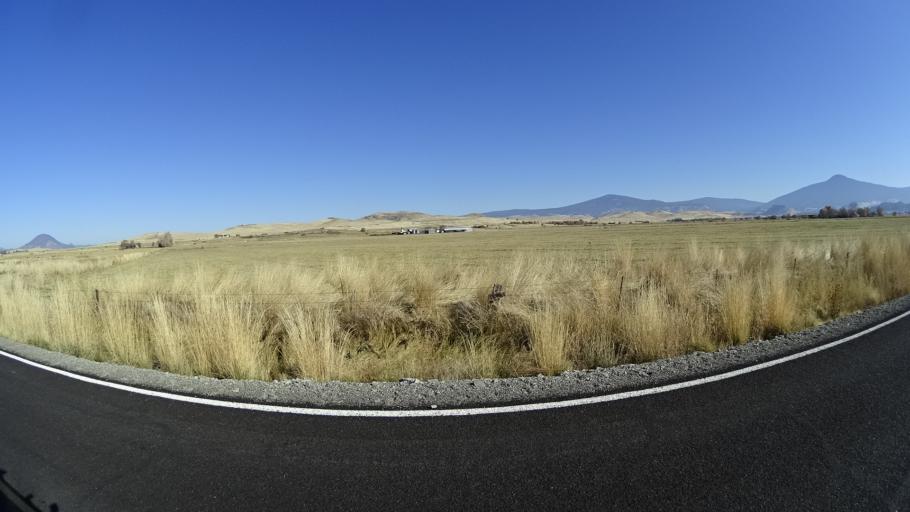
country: US
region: California
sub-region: Siskiyou County
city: Montague
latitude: 41.7166
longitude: -122.4464
